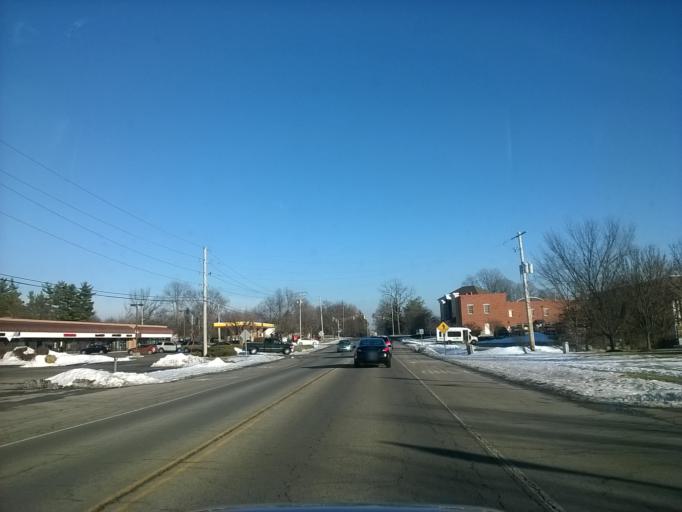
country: US
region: Indiana
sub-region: Hamilton County
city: Carmel
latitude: 39.9781
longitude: -86.1433
